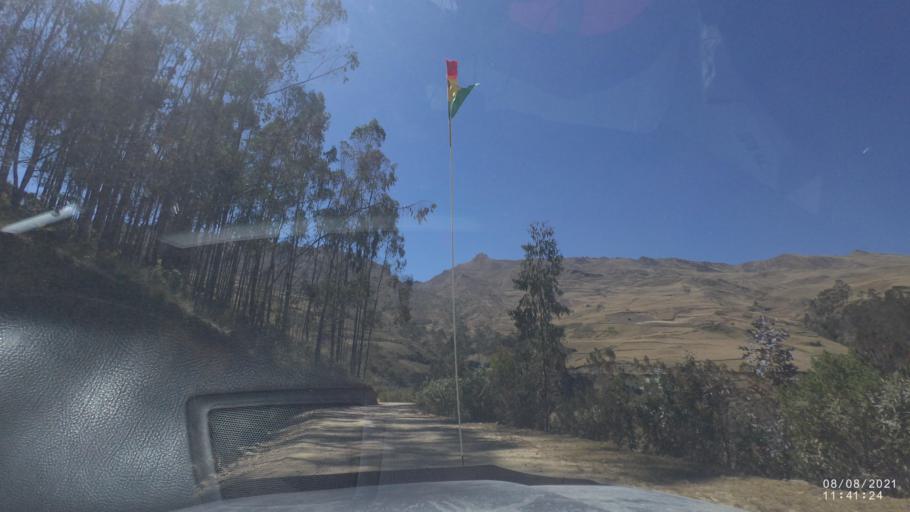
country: BO
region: Cochabamba
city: Colchani
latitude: -16.7966
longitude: -66.6425
